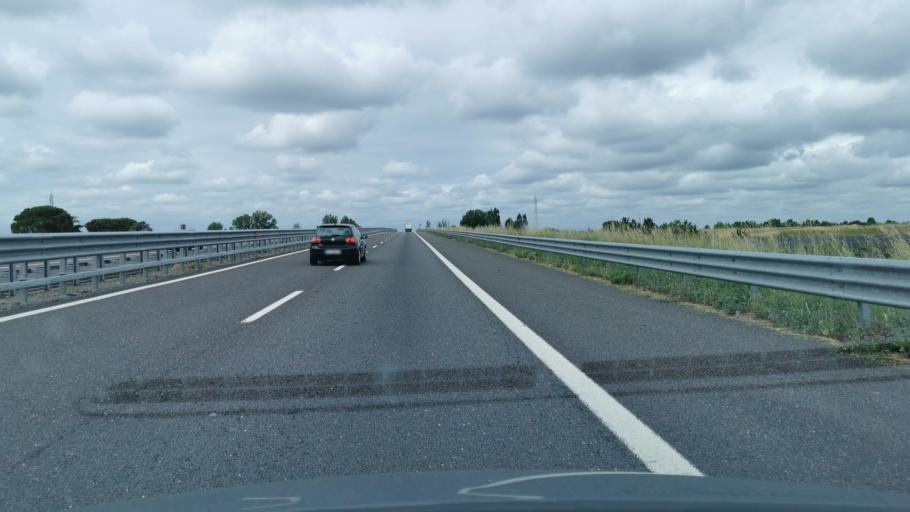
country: IT
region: Emilia-Romagna
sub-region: Provincia di Ravenna
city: Cotignola
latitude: 44.3967
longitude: 11.9497
